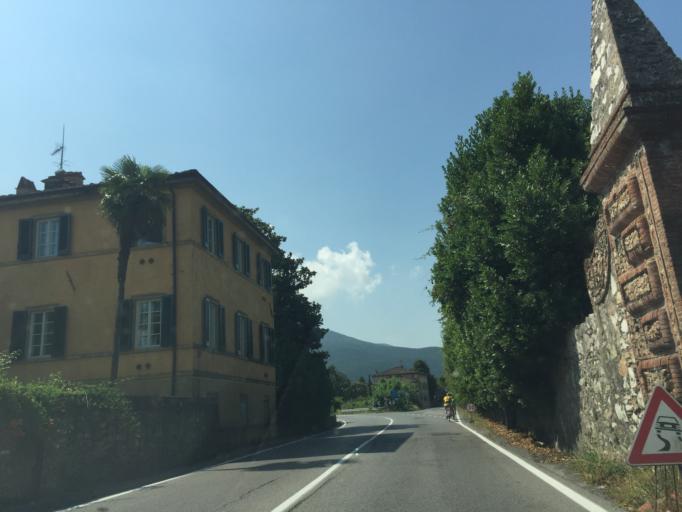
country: IT
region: Tuscany
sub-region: Provincia di Lucca
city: Lucca
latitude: 43.8049
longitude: 10.4843
